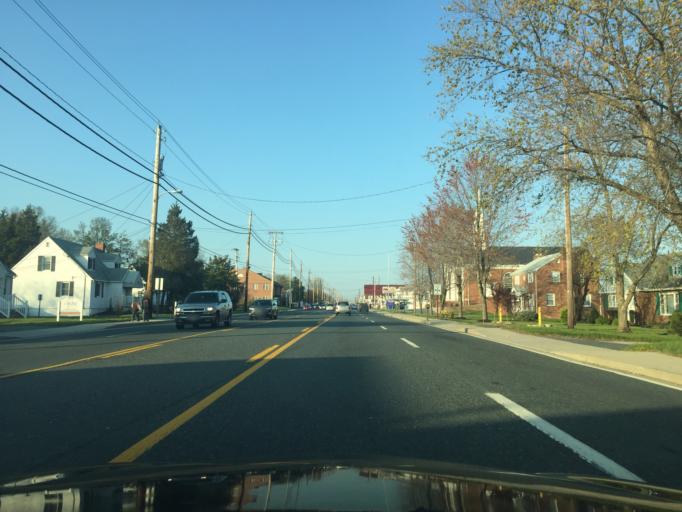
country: US
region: Maryland
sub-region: Baltimore County
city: Perry Hall
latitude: 39.4087
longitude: -76.4686
